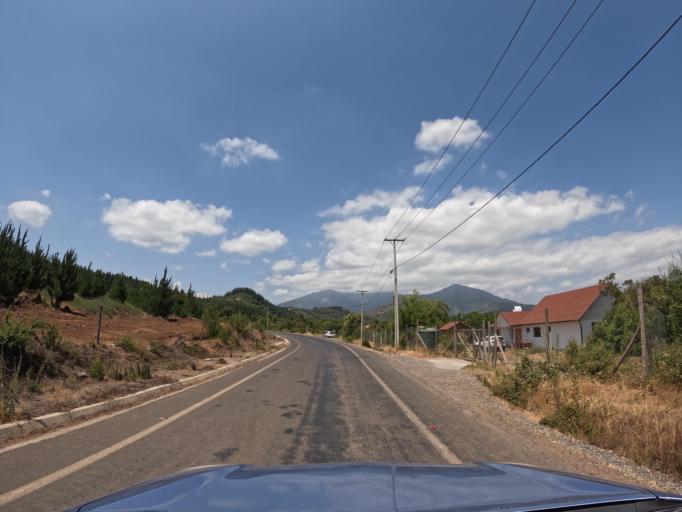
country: CL
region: Maule
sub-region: Provincia de Curico
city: Molina
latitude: -35.1779
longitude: -71.1062
